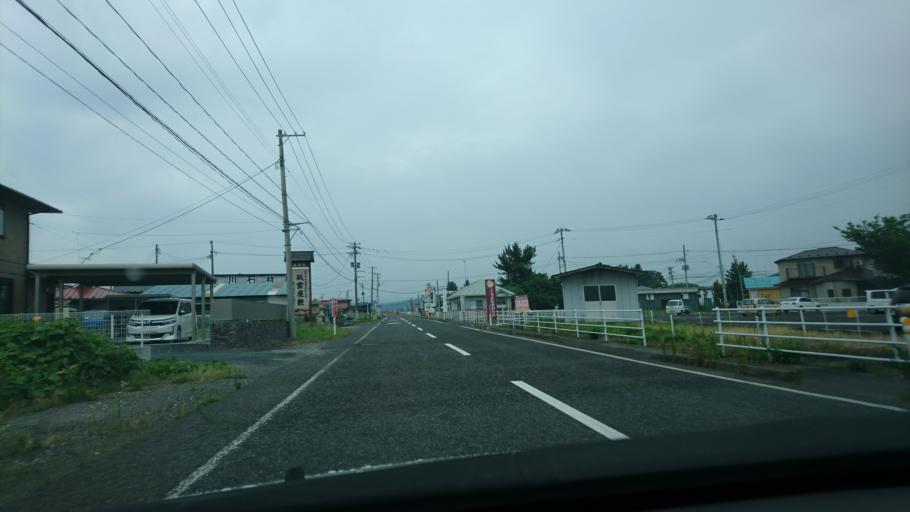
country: JP
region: Miyagi
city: Furukawa
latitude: 38.7380
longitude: 140.9501
